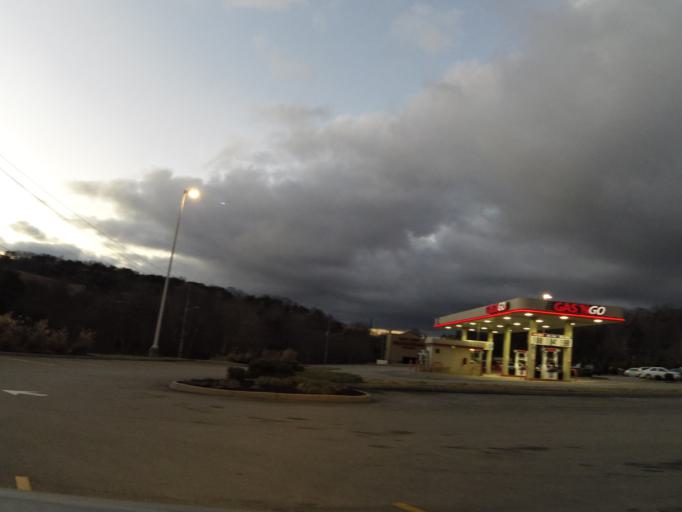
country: US
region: Tennessee
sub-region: Knox County
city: Knoxville
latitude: 36.0356
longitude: -83.8699
